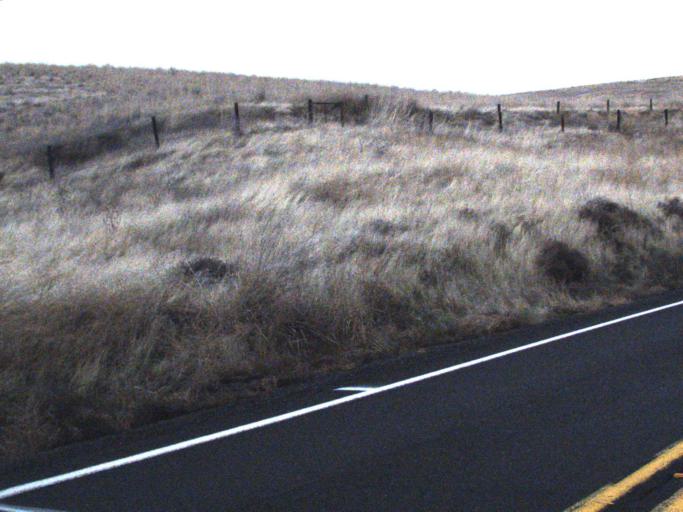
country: US
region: Washington
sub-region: Columbia County
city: Dayton
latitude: 46.4678
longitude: -117.9625
